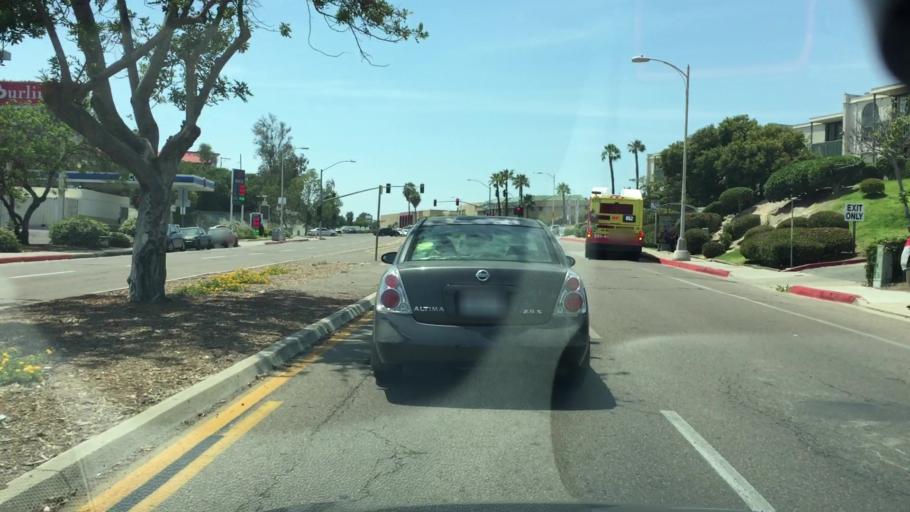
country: US
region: California
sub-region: San Diego County
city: Lemon Grove
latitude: 32.7483
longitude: -117.0779
